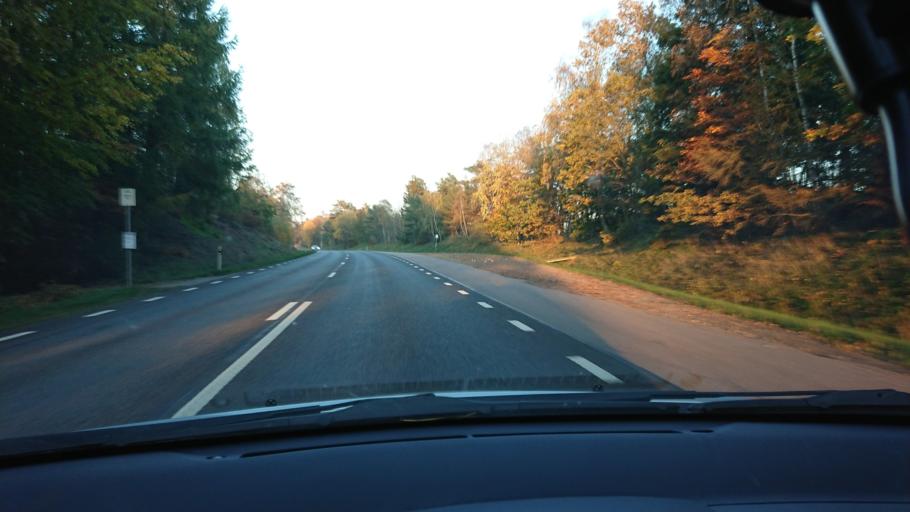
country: SE
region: Halland
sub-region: Halmstads Kommun
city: Aled
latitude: 56.7062
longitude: 13.0298
